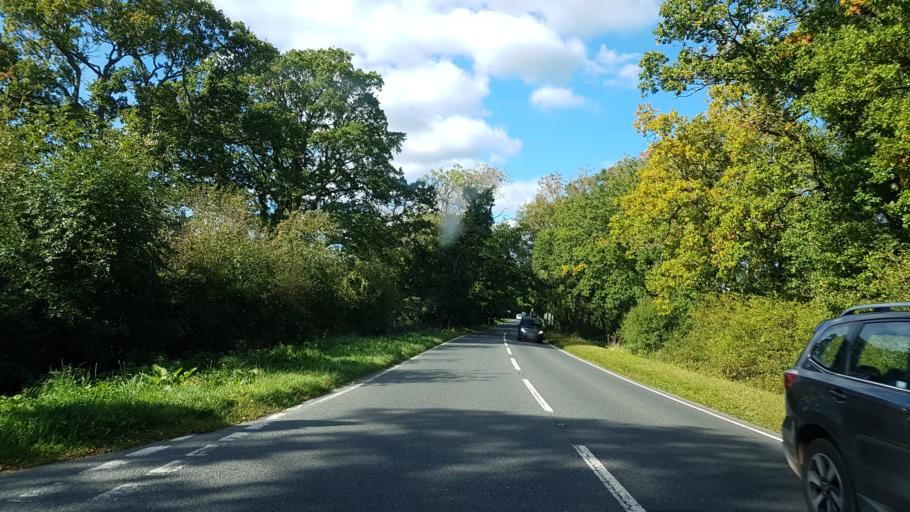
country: GB
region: England
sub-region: Surrey
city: Chiddingfold
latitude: 51.0770
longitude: -0.6475
